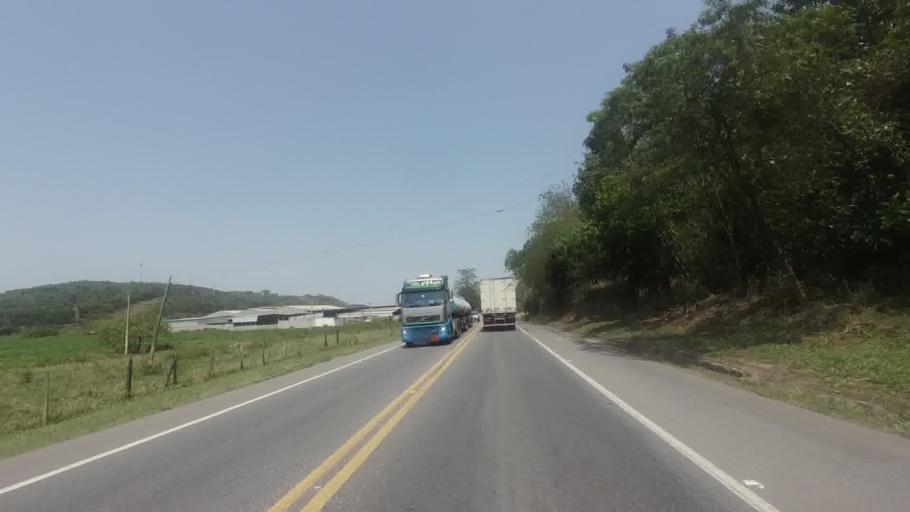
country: BR
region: Espirito Santo
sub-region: Iconha
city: Iconha
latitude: -20.8078
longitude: -40.8349
